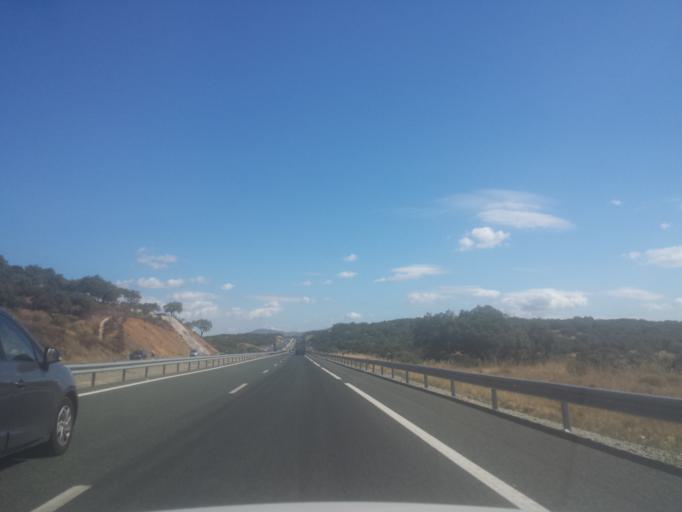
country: ES
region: Andalusia
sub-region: Provincia de Huelva
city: Santa Olalla del Cala
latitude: 37.8819
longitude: -6.2198
